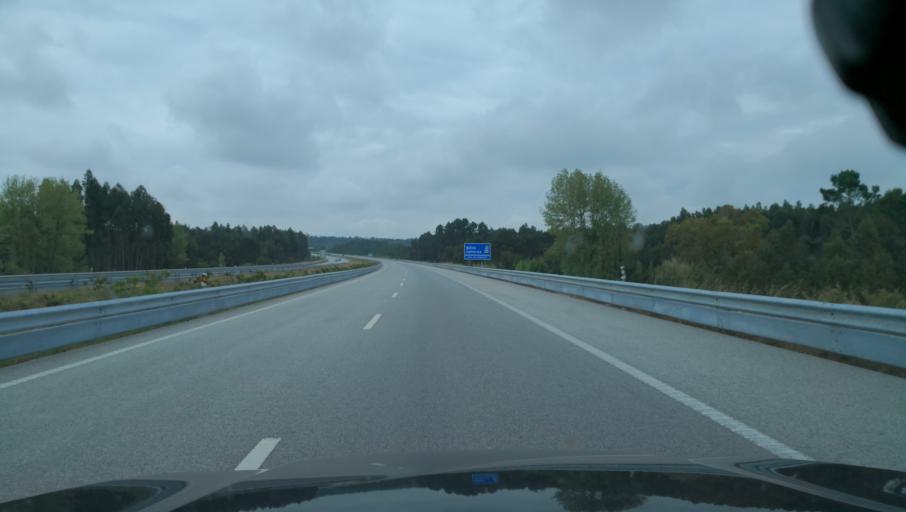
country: PT
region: Coimbra
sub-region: Figueira da Foz
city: Alhadas
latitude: 40.2057
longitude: -8.8142
